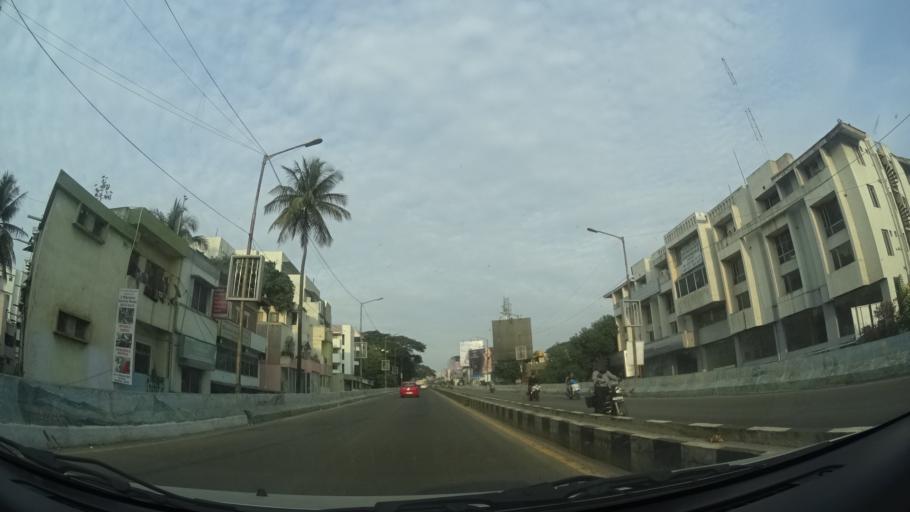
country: IN
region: Karnataka
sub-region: Bangalore Urban
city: Bangalore
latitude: 12.9959
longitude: 77.6202
